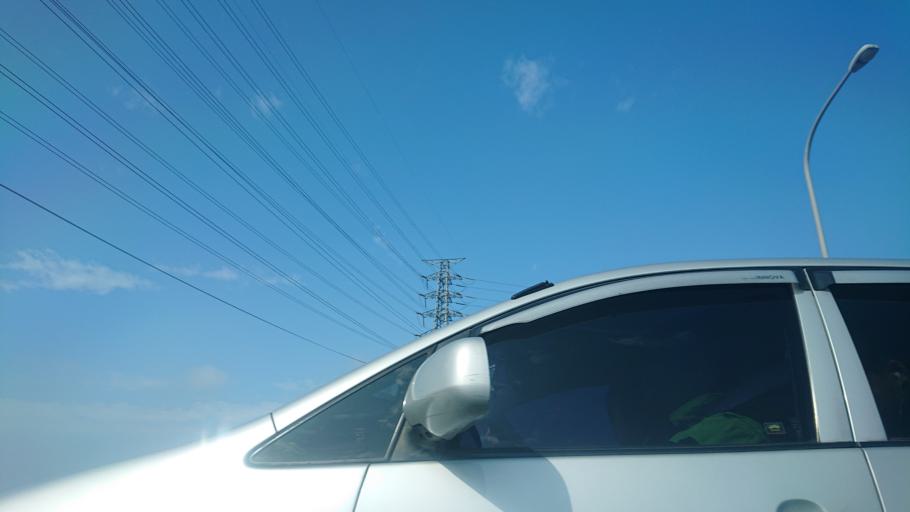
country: TW
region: Taiwan
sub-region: Changhua
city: Chang-hua
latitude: 24.0958
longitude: 120.4327
